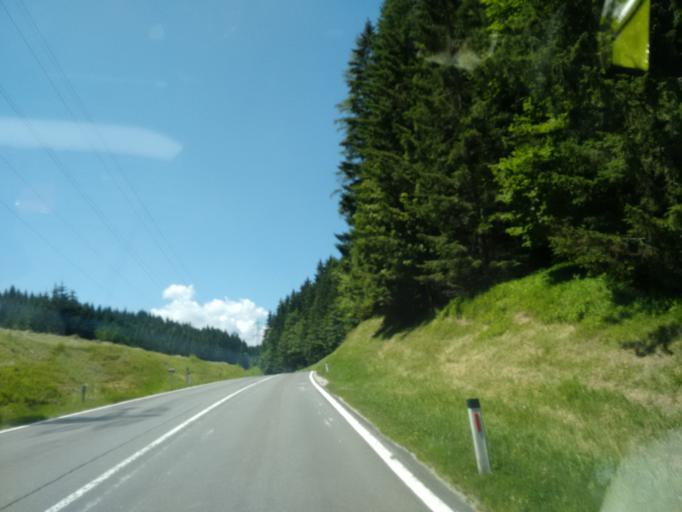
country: AT
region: Styria
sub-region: Politischer Bezirk Liezen
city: Altaussee
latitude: 47.6272
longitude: 13.7124
